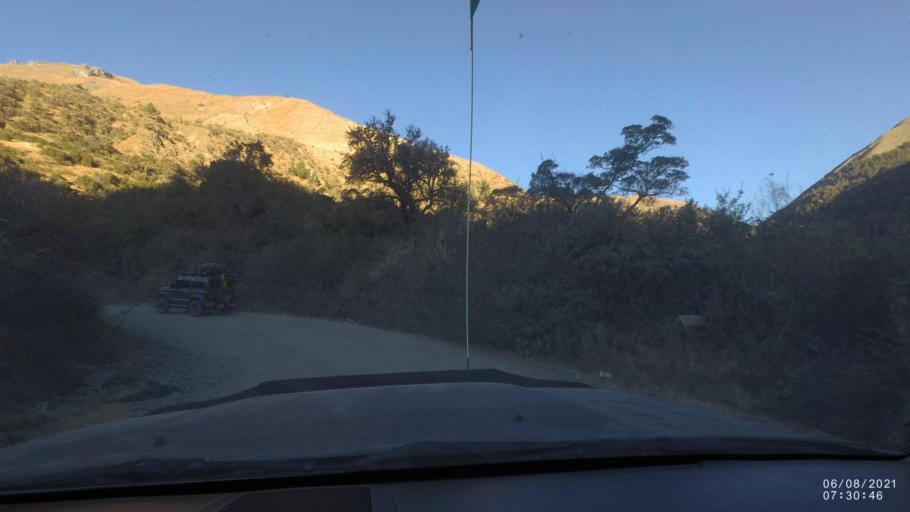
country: BO
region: Cochabamba
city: Sipe Sipe
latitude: -17.2772
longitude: -66.3217
